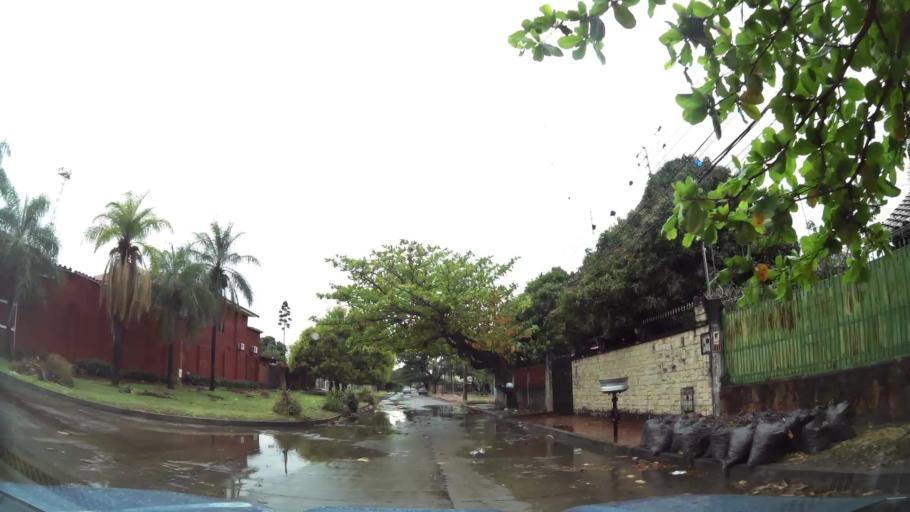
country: BO
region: Santa Cruz
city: Santa Cruz de la Sierra
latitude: -17.8086
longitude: -63.1664
